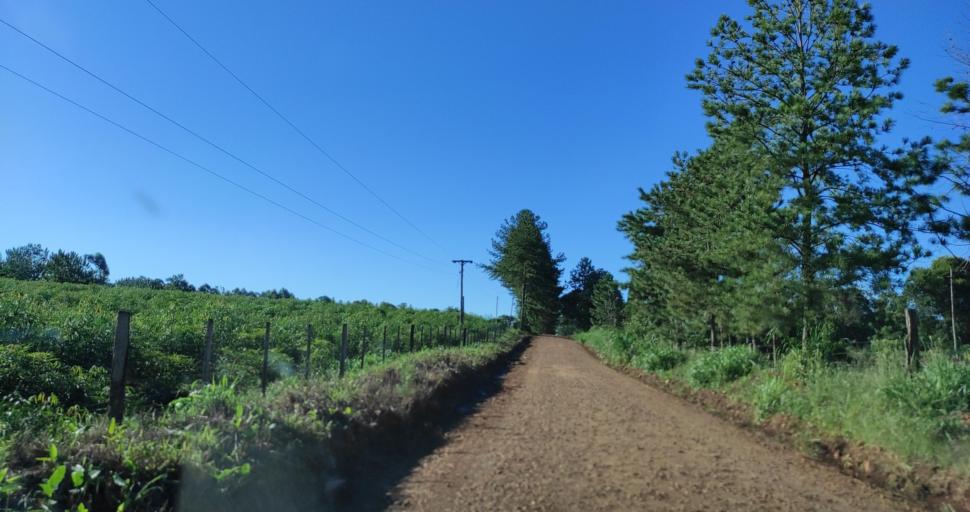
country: AR
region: Misiones
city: Garuhape
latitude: -26.8510
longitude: -55.0034
